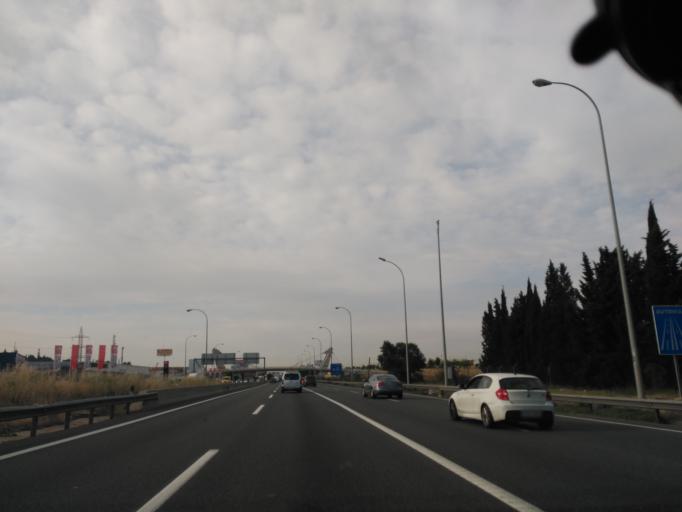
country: ES
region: Madrid
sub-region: Provincia de Madrid
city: Villaverde
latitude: 40.3219
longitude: -3.6923
